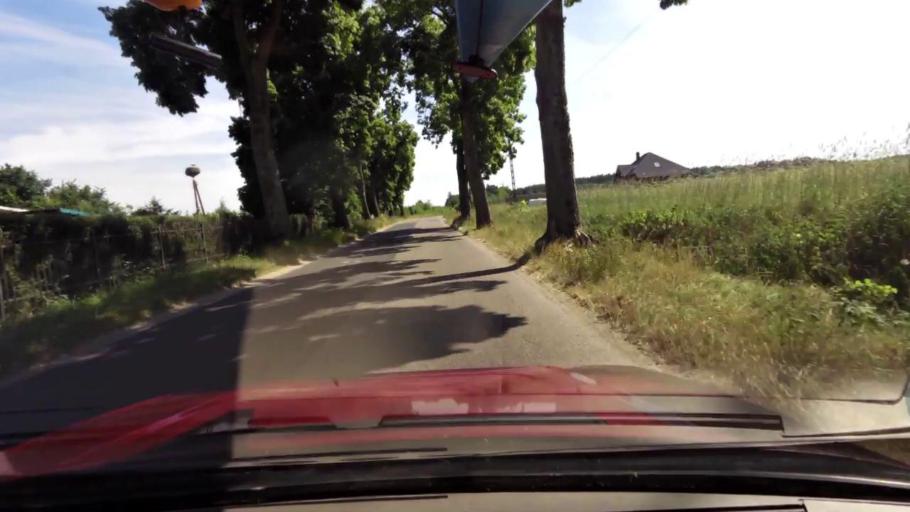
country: PL
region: Pomeranian Voivodeship
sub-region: Powiat slupski
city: Kobylnica
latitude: 54.3780
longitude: 16.9655
